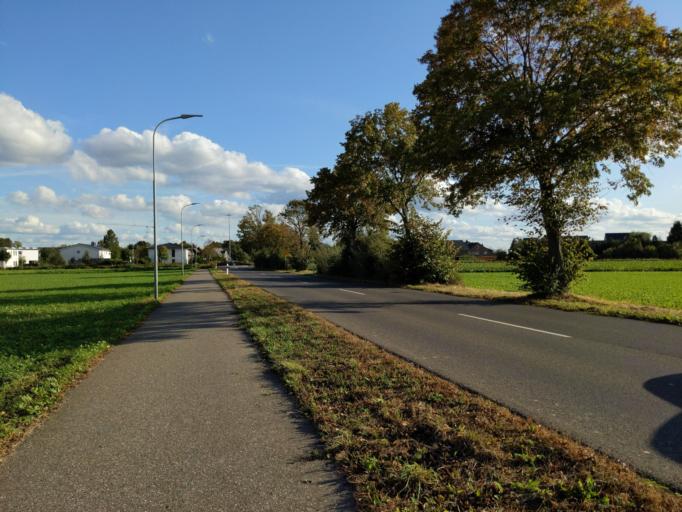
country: DE
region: North Rhine-Westphalia
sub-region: Regierungsbezirk Dusseldorf
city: Kaarst
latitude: 51.2104
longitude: 6.5881
